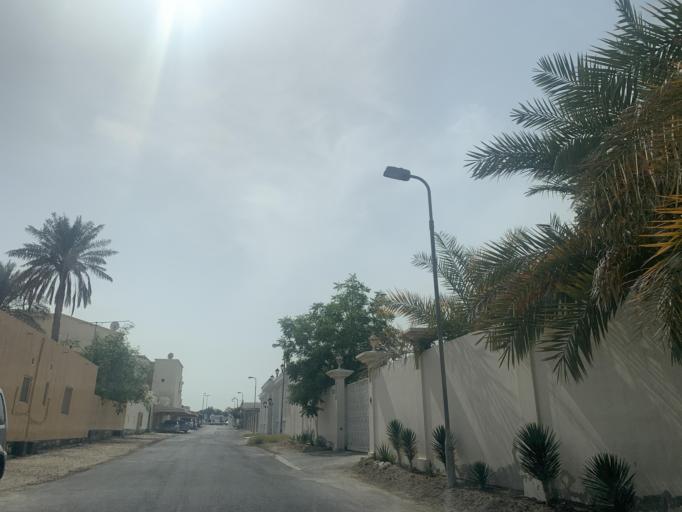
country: BH
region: Northern
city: Ar Rifa'
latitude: 26.1318
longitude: 50.5479
